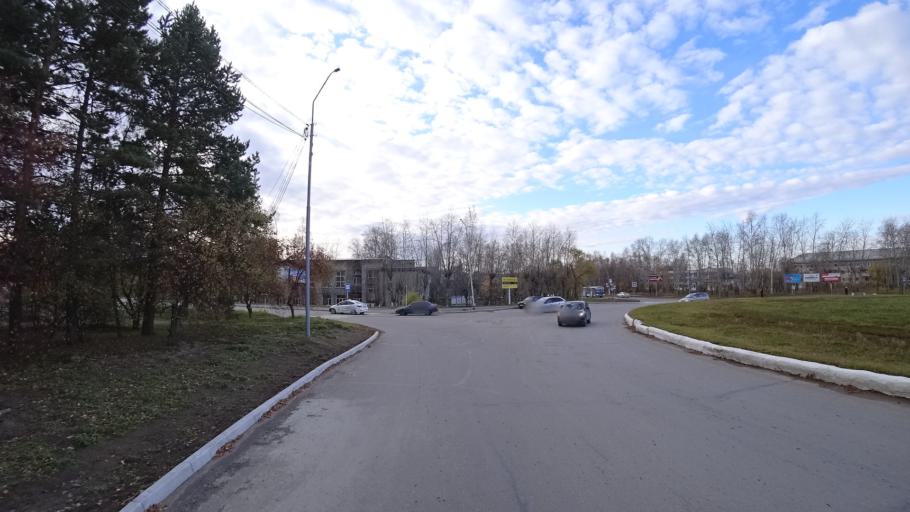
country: RU
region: Khabarovsk Krai
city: Amursk
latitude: 50.2300
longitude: 136.9021
